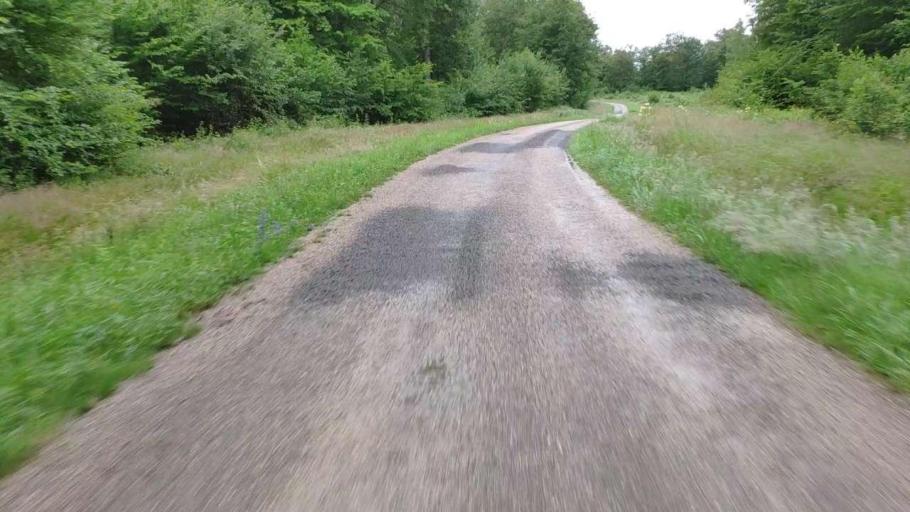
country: FR
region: Franche-Comte
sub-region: Departement du Jura
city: Chaussin
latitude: 46.8863
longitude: 5.4206
